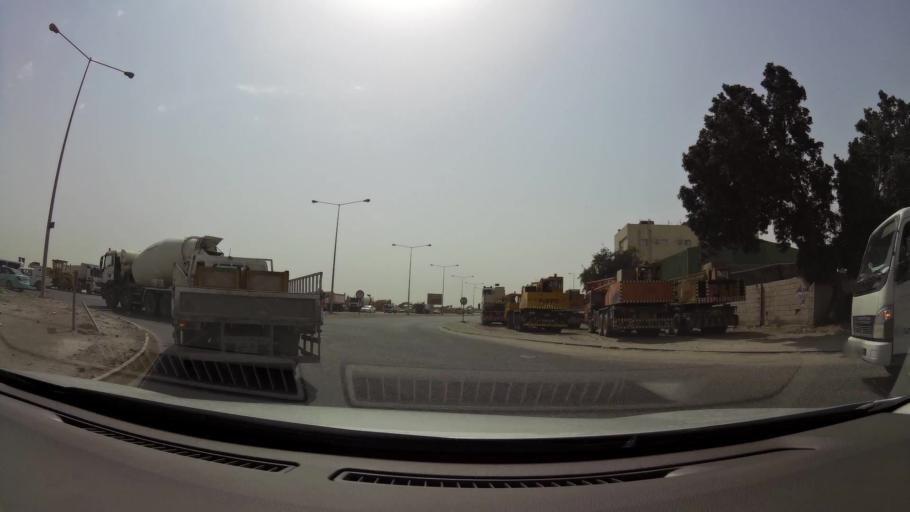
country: QA
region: Al Wakrah
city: Al Wukayr
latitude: 25.1780
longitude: 51.4653
